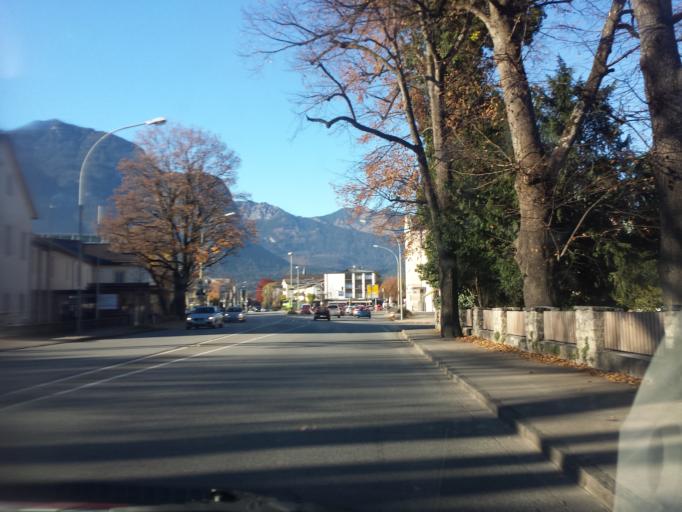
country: DE
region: Bavaria
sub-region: Upper Bavaria
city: Garmisch-Partenkirchen
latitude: 47.4930
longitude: 11.1067
